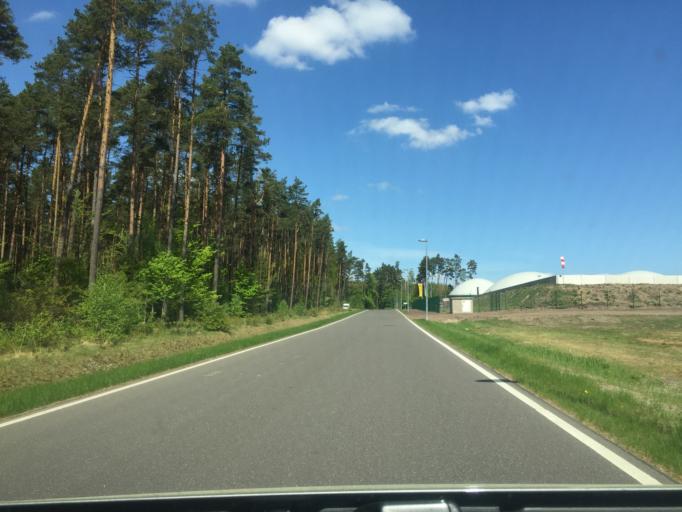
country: DE
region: Mecklenburg-Vorpommern
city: Torgelow
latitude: 53.6351
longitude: 13.9873
